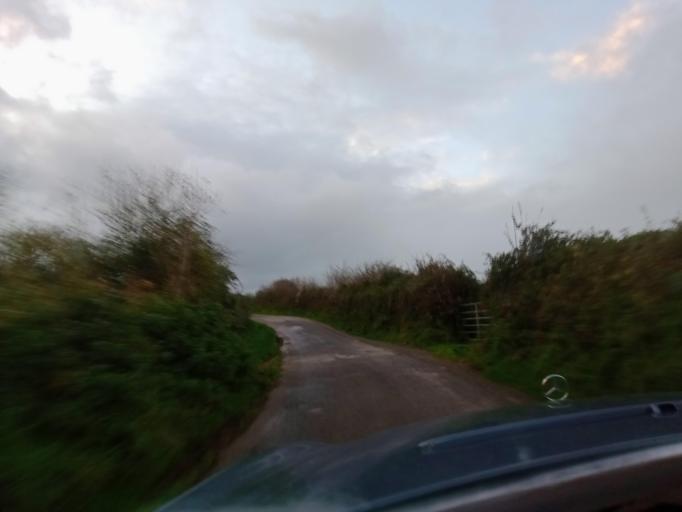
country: IE
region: Munster
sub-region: Waterford
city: Waterford
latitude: 52.3320
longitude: -7.0294
